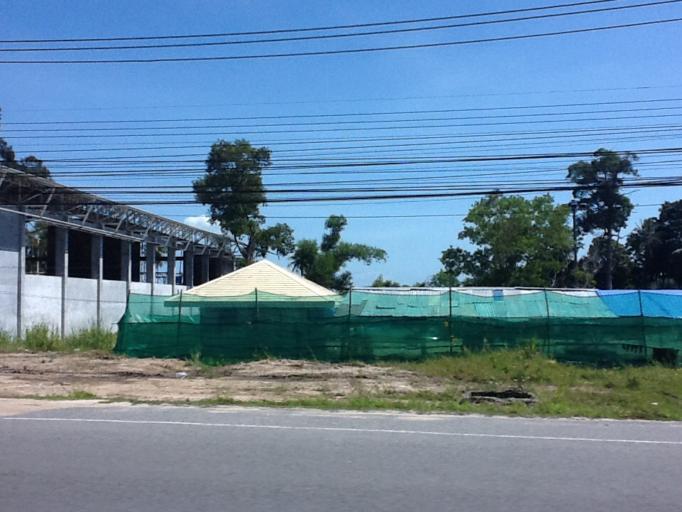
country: TH
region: Phuket
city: Thalang
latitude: 8.0130
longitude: 98.3987
